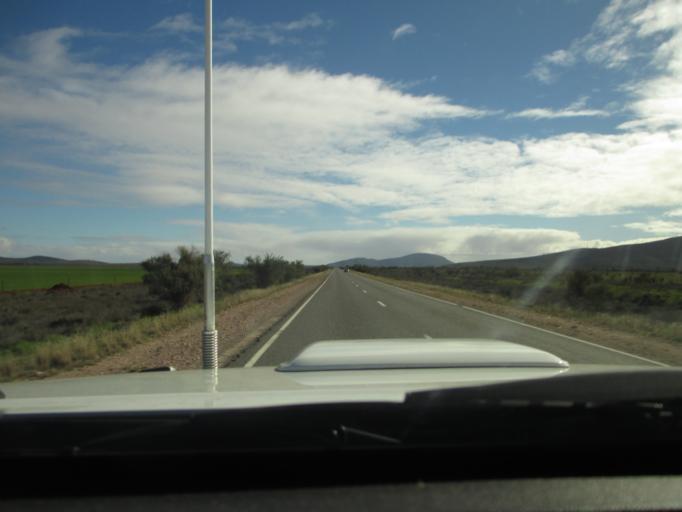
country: AU
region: South Australia
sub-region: Flinders Ranges
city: Quorn
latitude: -31.8638
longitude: 138.4045
